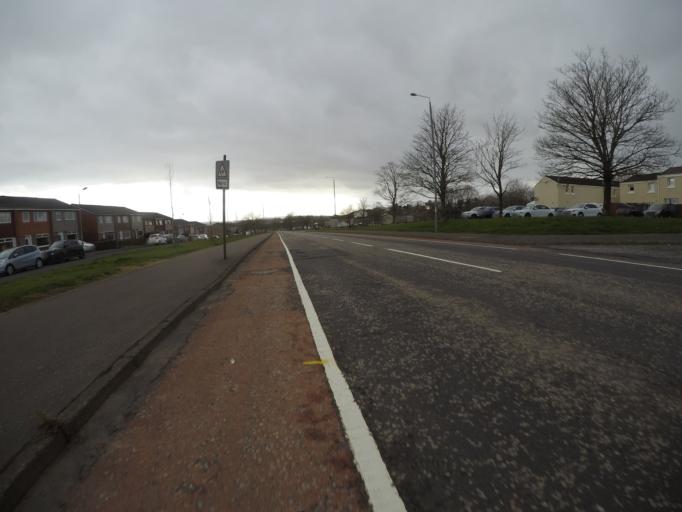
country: GB
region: Scotland
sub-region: East Ayrshire
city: Kilmarnock
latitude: 55.6209
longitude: -4.4725
